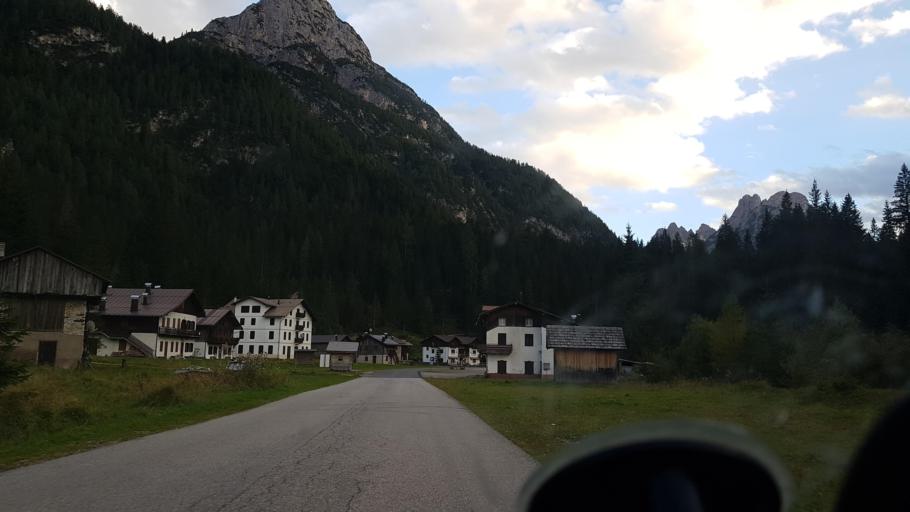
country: IT
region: Veneto
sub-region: Provincia di Belluno
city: San Pietro di Cadore
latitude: 46.6036
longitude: 12.6305
